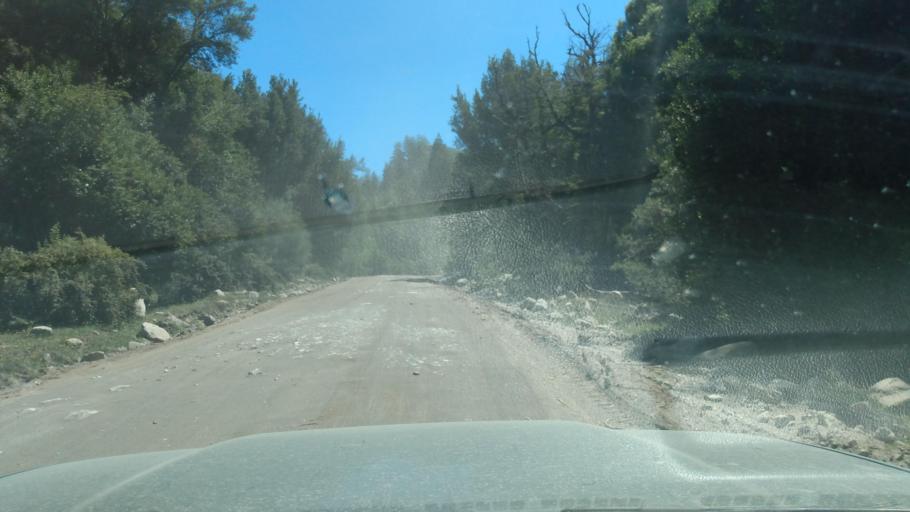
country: AR
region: Neuquen
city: Villa La Angostura
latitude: -40.6167
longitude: -71.5312
